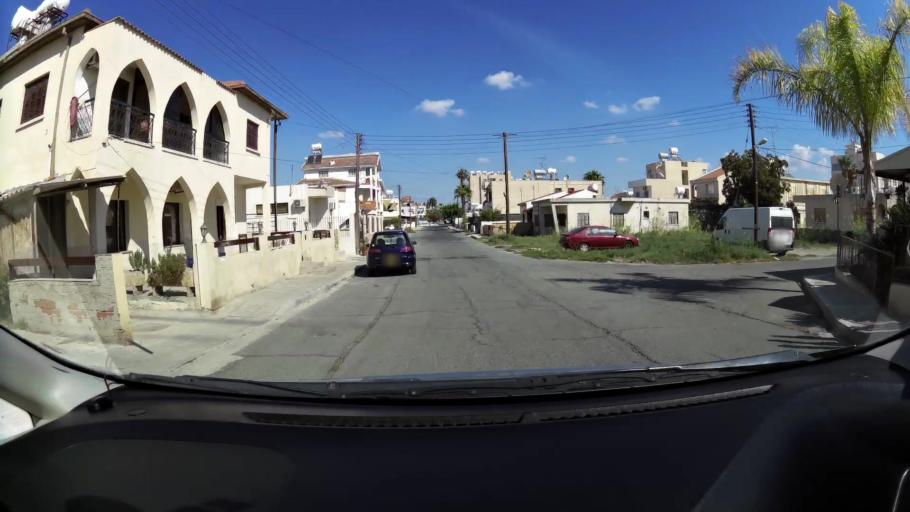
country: CY
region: Larnaka
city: Larnaca
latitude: 34.9243
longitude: 33.6294
